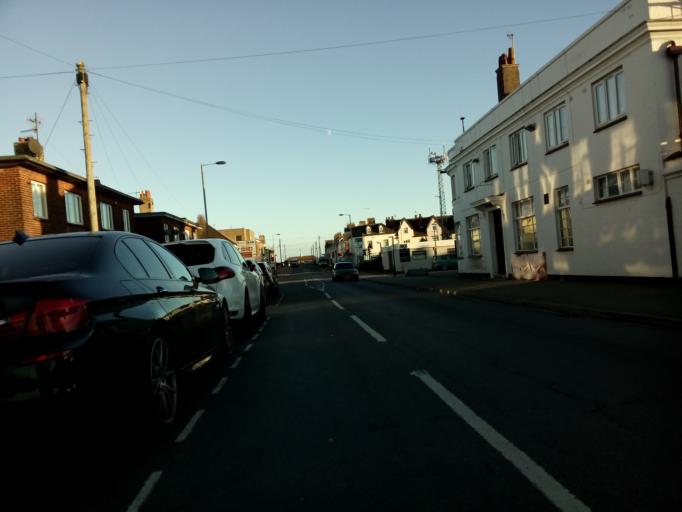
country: GB
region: England
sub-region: Suffolk
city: Felixstowe
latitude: 51.9529
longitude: 1.3346
